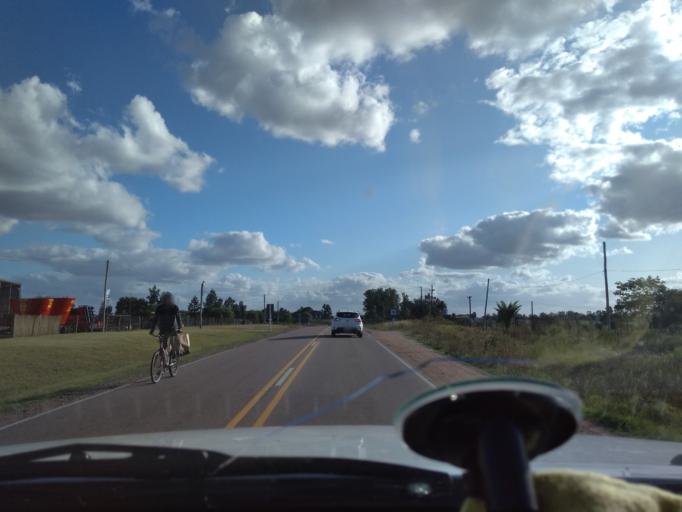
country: UY
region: Canelones
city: Tala
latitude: -34.3683
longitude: -55.7823
